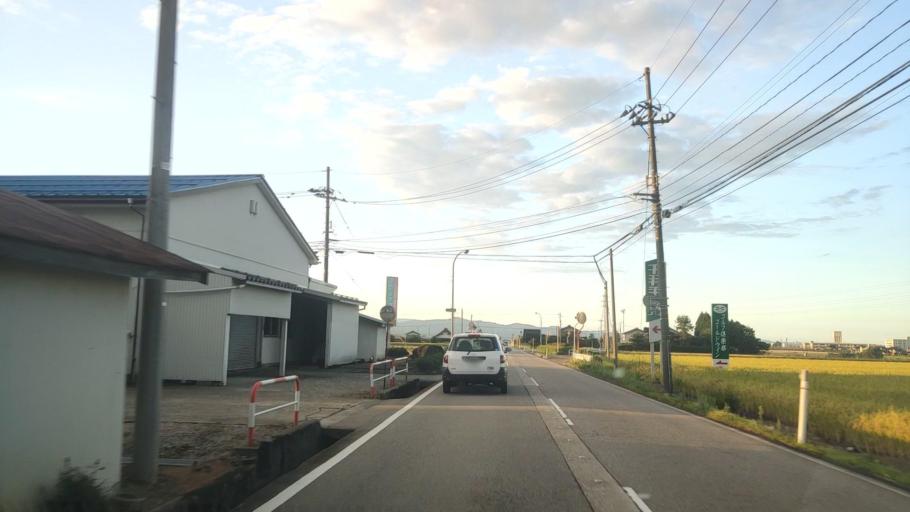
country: JP
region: Toyama
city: Nanto-shi
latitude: 36.6162
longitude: 136.8896
